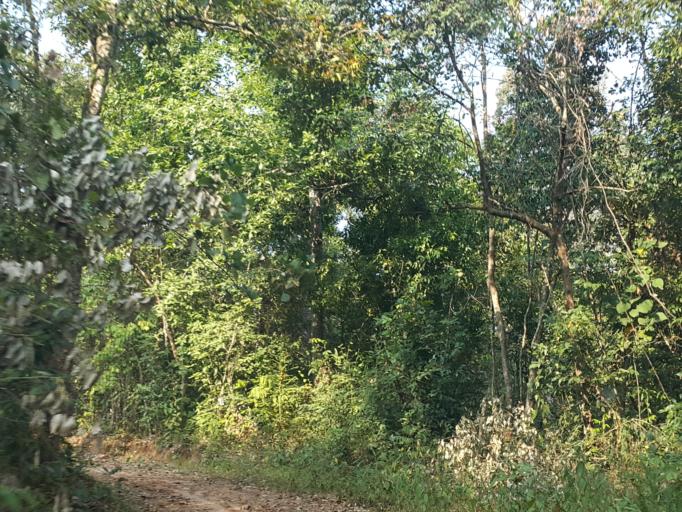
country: TH
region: Chiang Mai
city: Samoeng
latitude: 19.0214
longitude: 98.7614
